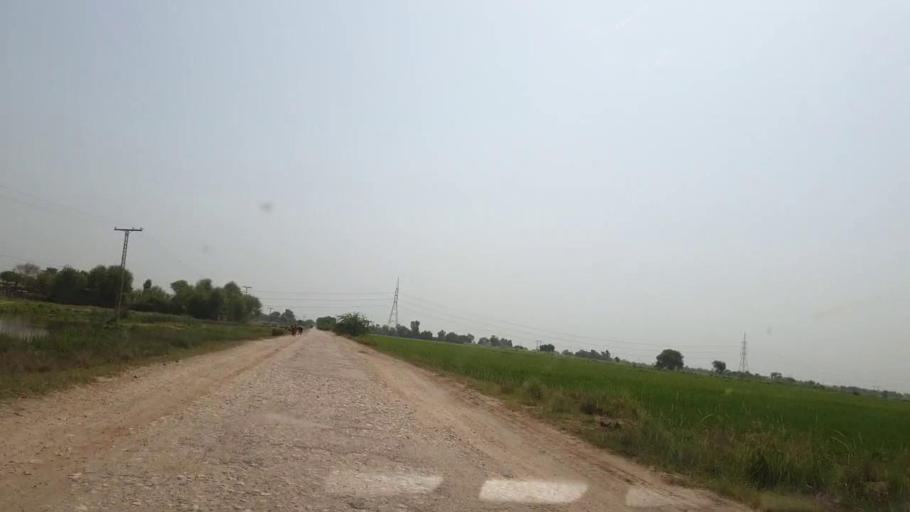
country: PK
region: Sindh
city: Lakhi
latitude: 27.8796
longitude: 68.6730
